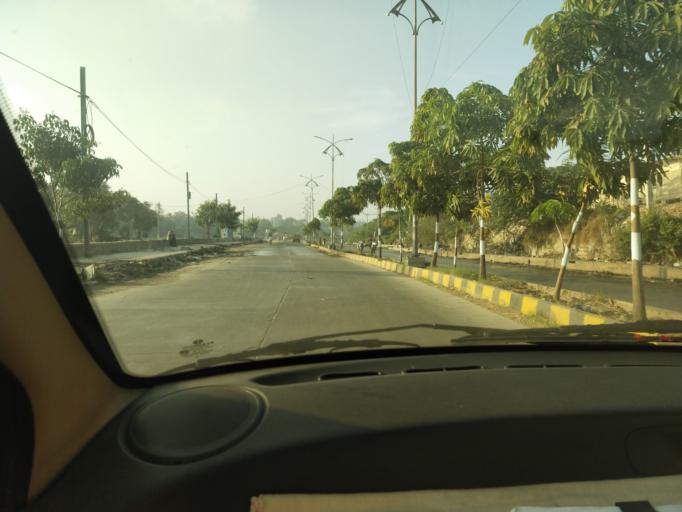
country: IN
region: Telangana
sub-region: Hyderabad
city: Hyderabad
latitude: 17.3654
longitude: 78.4555
